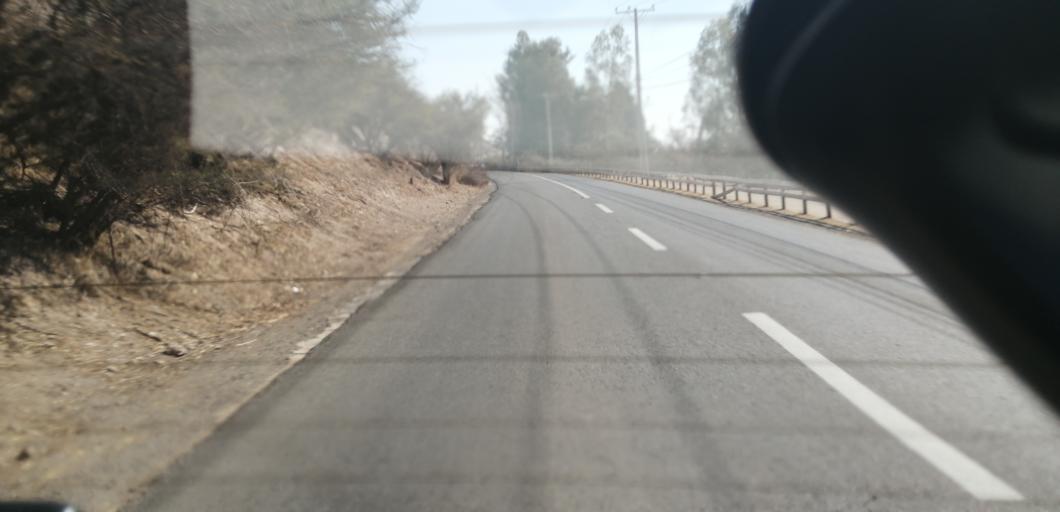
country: CL
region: Santiago Metropolitan
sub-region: Provincia de Santiago
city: Lo Prado
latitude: -33.4449
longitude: -70.8250
